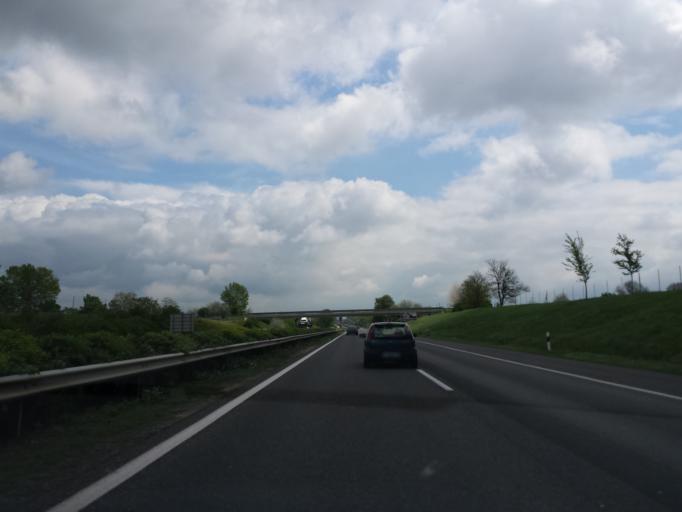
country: HU
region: Komarom-Esztergom
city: Kocs
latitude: 47.6324
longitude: 18.2493
